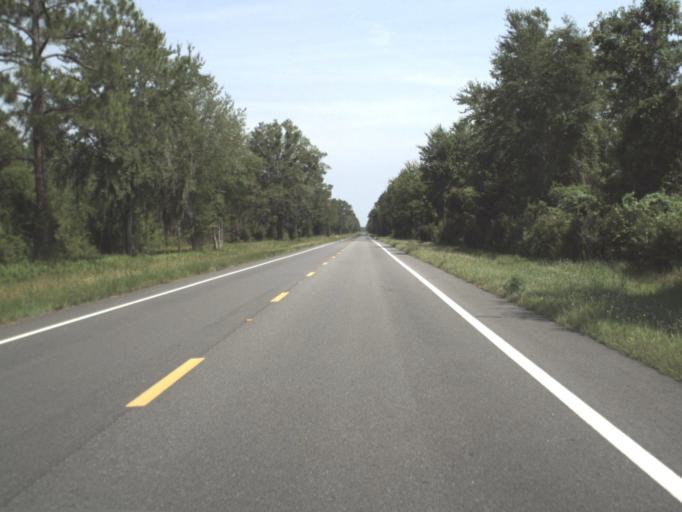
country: US
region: Florida
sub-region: Hamilton County
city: Jasper
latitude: 30.5823
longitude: -83.0001
